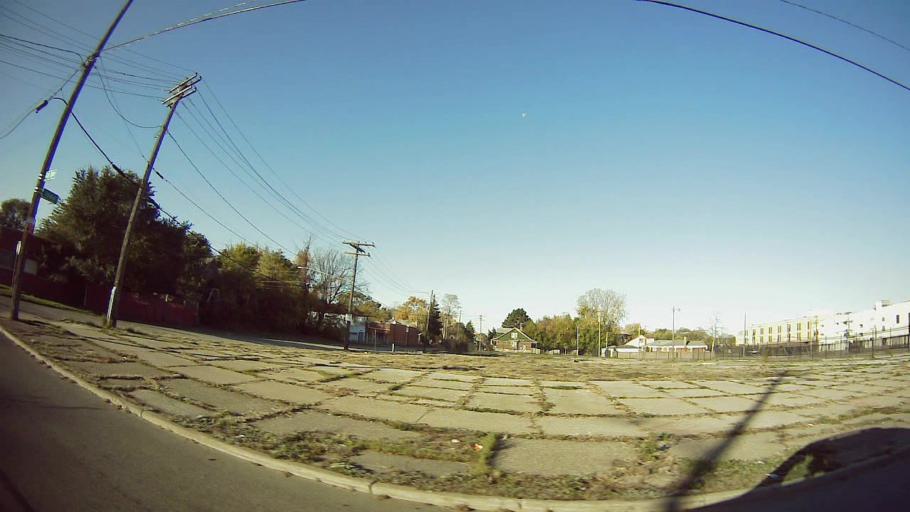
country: US
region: Michigan
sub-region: Wayne County
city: Hamtramck
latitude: 42.4256
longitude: -83.0241
